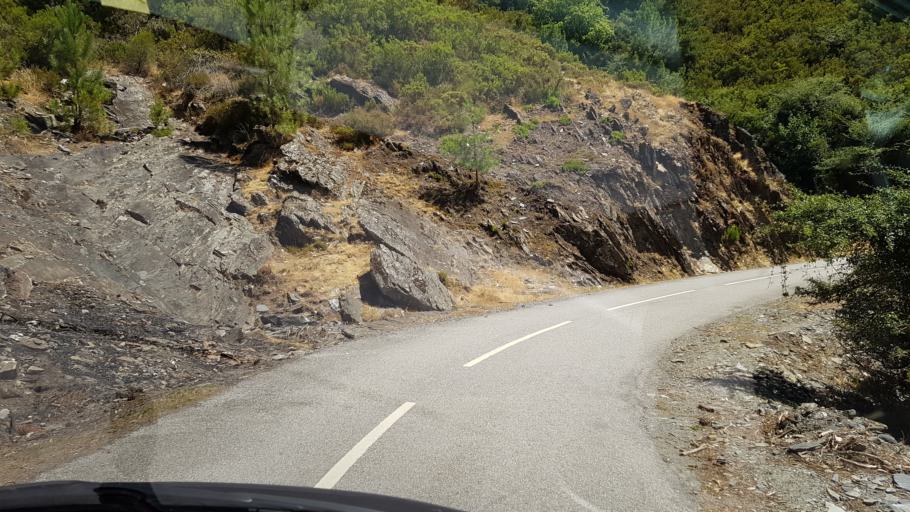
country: PT
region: Vila Real
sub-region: Mondim de Basto
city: Mondim de Basto
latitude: 41.3334
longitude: -7.8806
